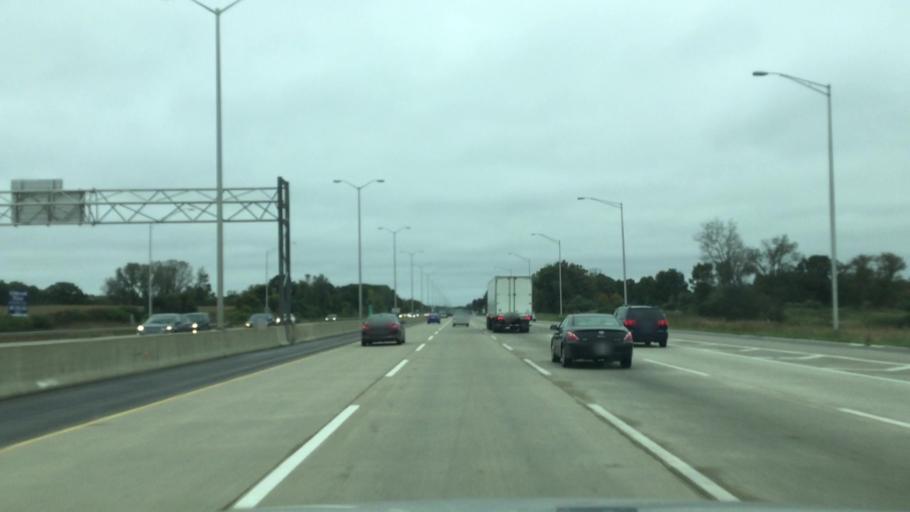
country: US
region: Illinois
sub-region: Lake County
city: Wadsworth
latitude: 42.4620
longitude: -87.9628
